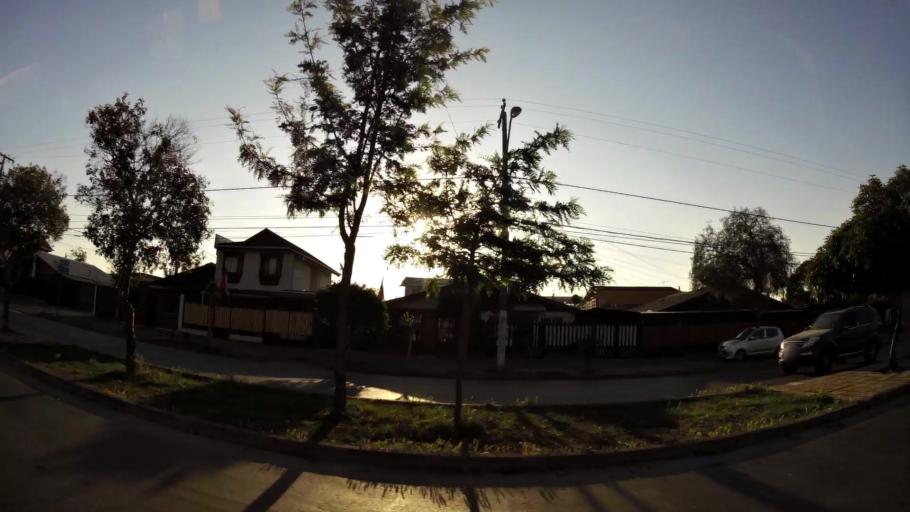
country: CL
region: Santiago Metropolitan
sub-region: Provincia de Santiago
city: La Pintana
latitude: -33.5455
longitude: -70.6247
